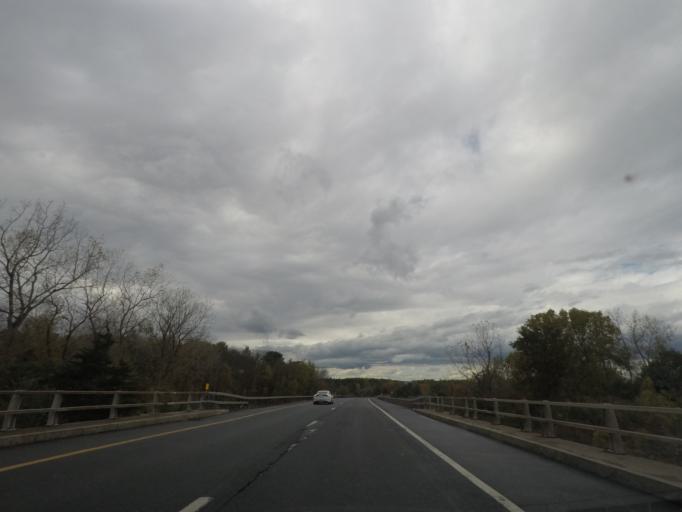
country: US
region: New York
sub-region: Columbia County
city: Niverville
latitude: 42.4870
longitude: -73.6972
